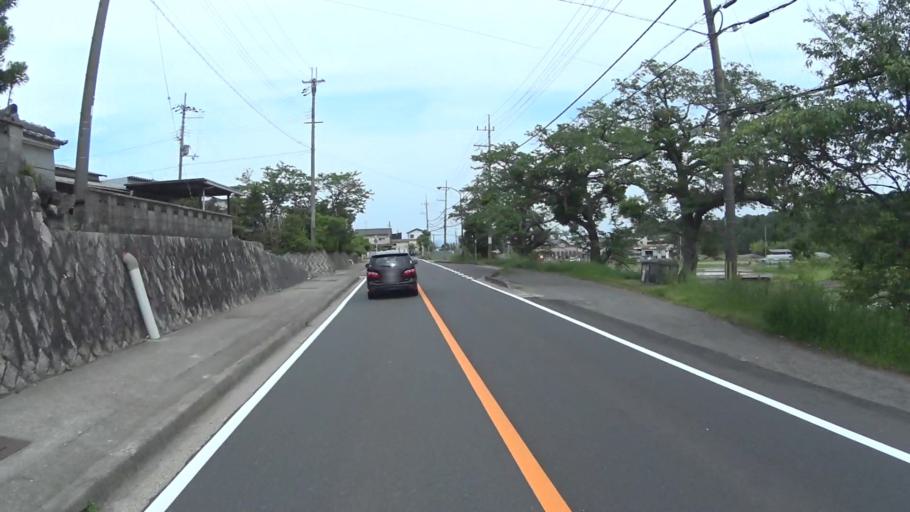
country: JP
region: Shiga Prefecture
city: Kitahama
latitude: 35.1332
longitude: 135.8962
